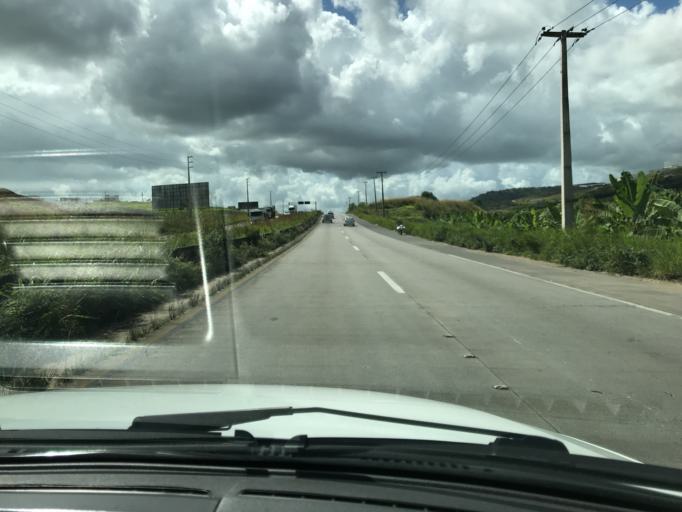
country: BR
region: Pernambuco
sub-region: Vitoria De Santo Antao
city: Vitoria de Santo Antao
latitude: -8.1261
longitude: -35.2776
